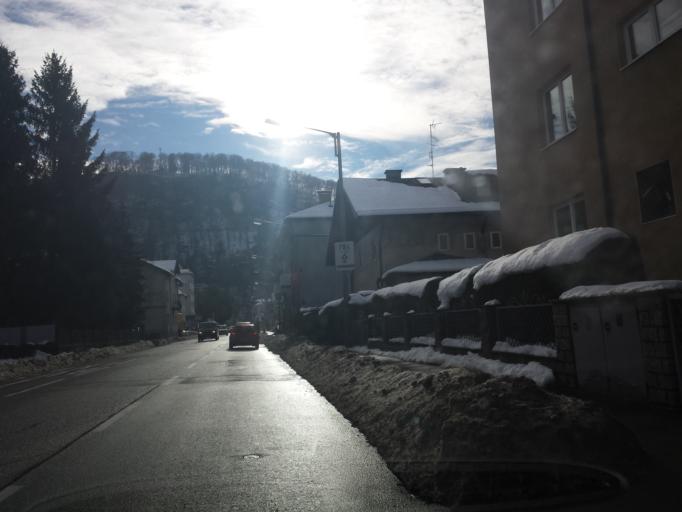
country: AT
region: Salzburg
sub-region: Salzburg Stadt
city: Salzburg
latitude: 47.8123
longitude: 13.0543
